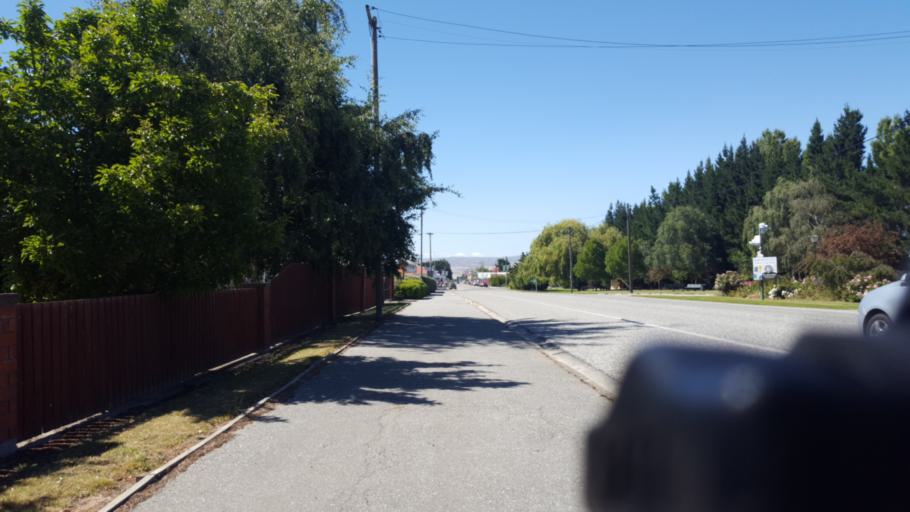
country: NZ
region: Otago
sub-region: Dunedin City
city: Dunedin
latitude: -45.1271
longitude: 170.0966
